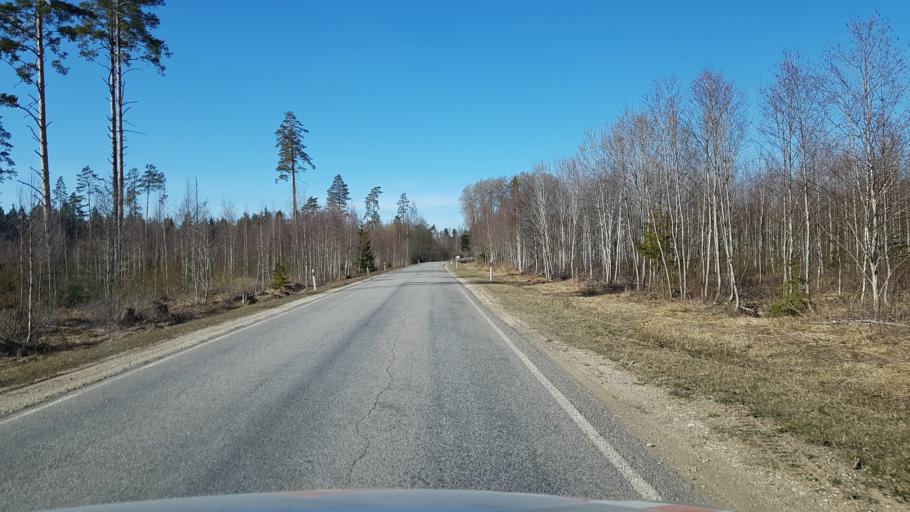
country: EE
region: Laeaene-Virumaa
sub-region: Vinni vald
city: Vinni
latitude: 59.2445
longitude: 26.6901
